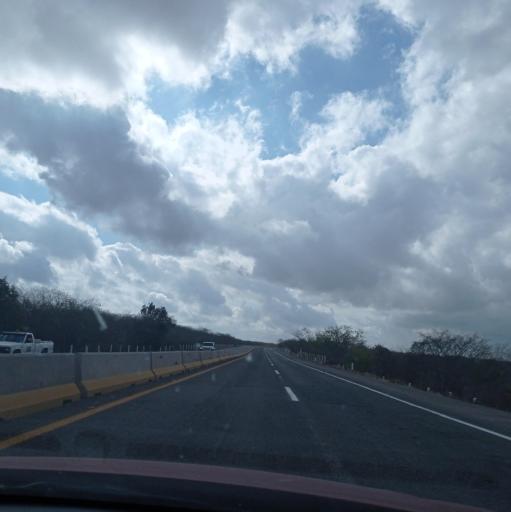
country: MX
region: Sinaloa
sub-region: Navolato
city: Juan Aldama (El Tigre)
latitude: 24.9957
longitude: -107.7778
